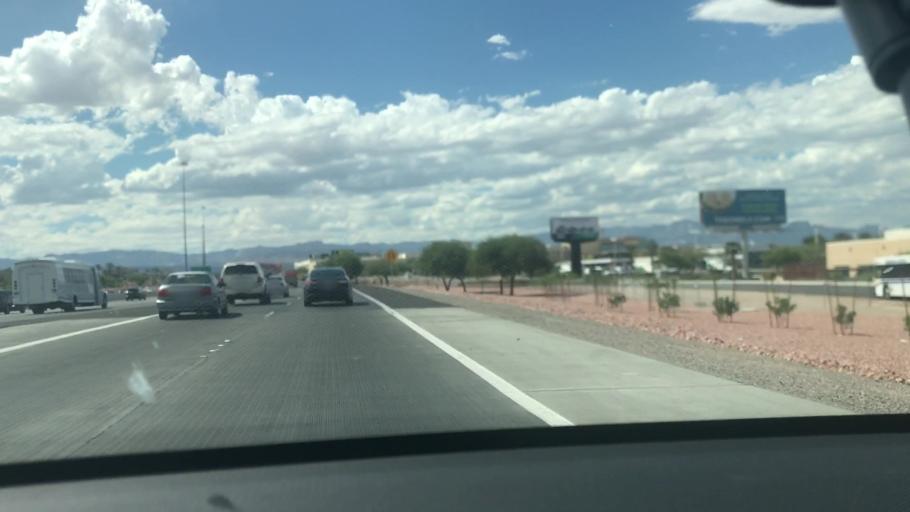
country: US
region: Nevada
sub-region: Clark County
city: Paradise
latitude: 36.0637
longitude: -115.1529
